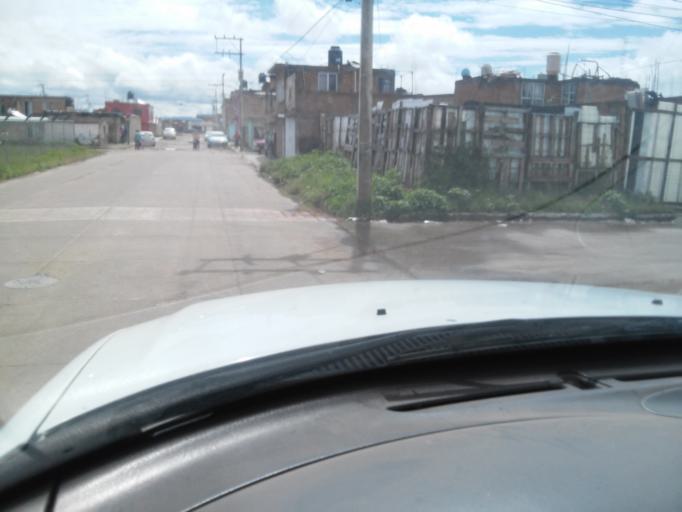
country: MX
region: Durango
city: Victoria de Durango
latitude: 24.0166
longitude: -104.6076
